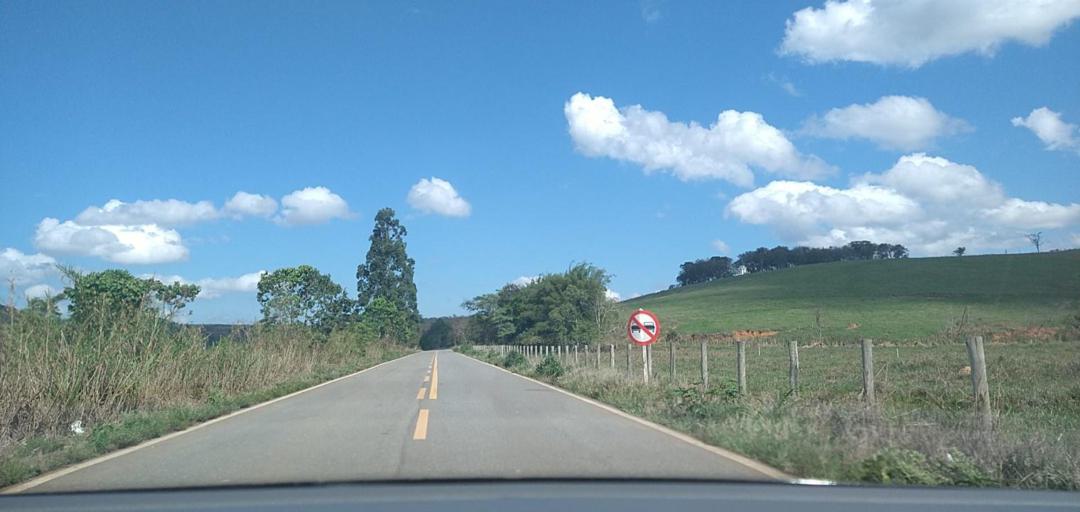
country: BR
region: Minas Gerais
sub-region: Alvinopolis
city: Alvinopolis
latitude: -20.0162
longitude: -43.0814
